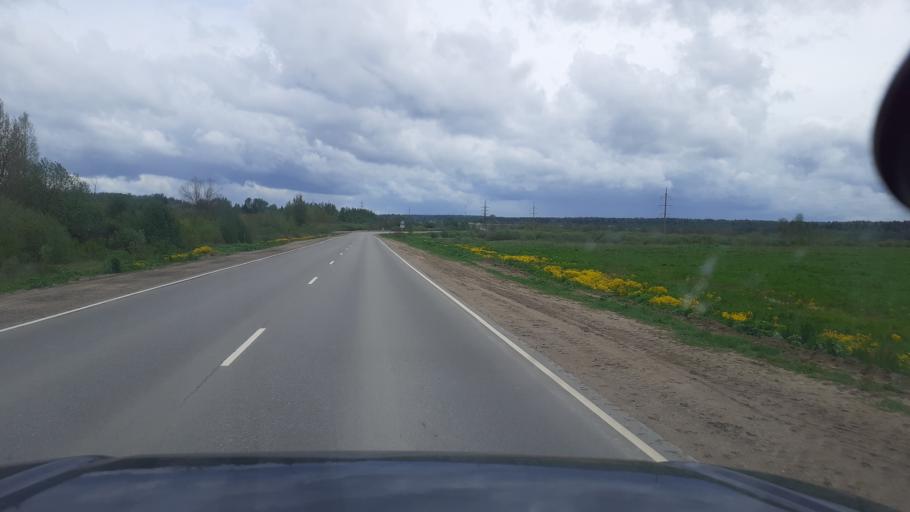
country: RU
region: Moskovskaya
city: Sychevo
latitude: 55.9847
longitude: 36.2196
